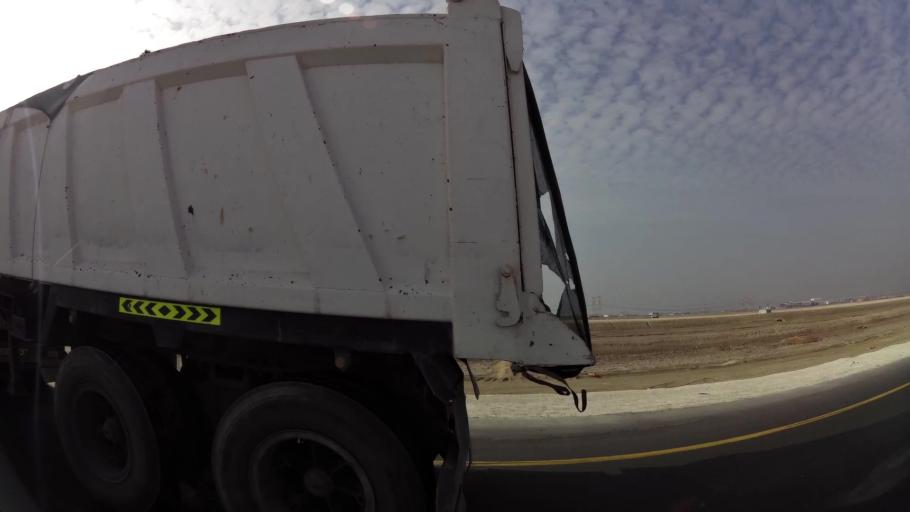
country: AE
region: Abu Dhabi
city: Abu Dhabi
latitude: 24.2563
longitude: 54.4833
